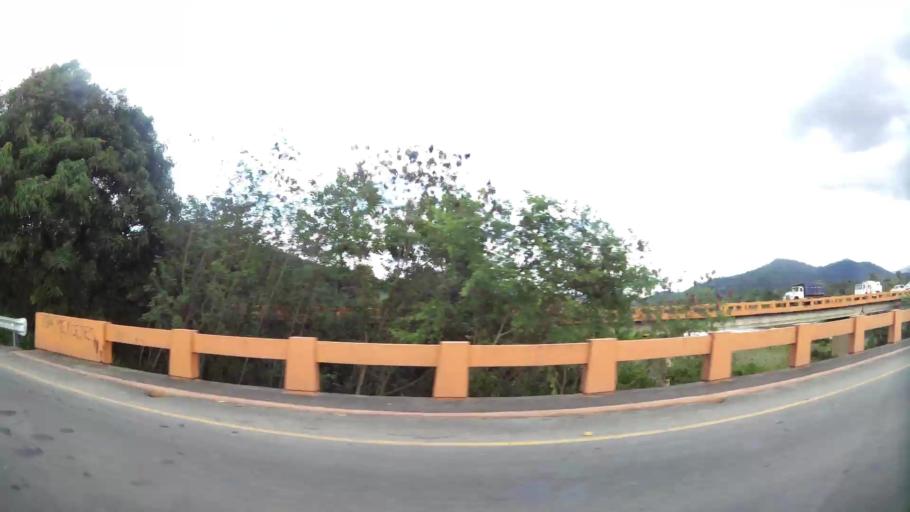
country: DO
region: Monsenor Nouel
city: Bonao
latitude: 18.9613
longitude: -70.4064
